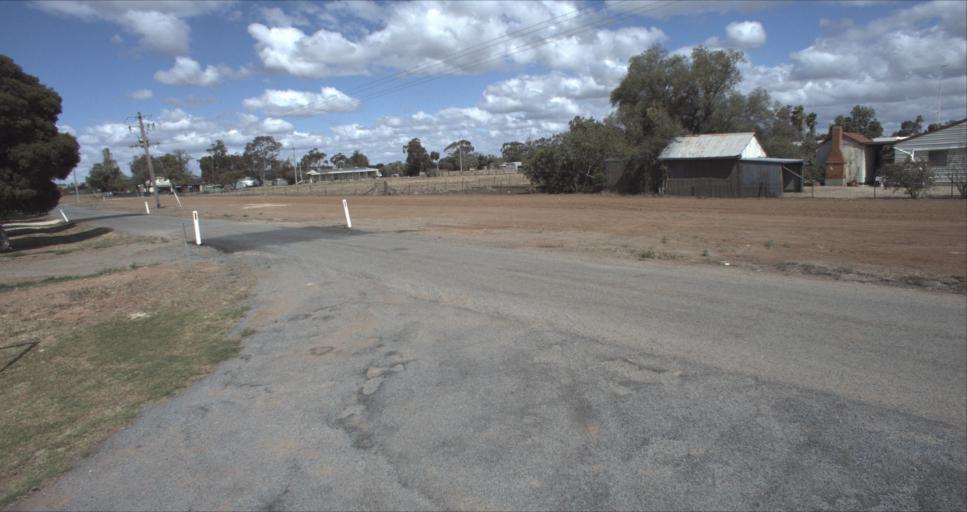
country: AU
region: New South Wales
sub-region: Leeton
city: Leeton
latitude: -34.5940
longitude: 146.4102
